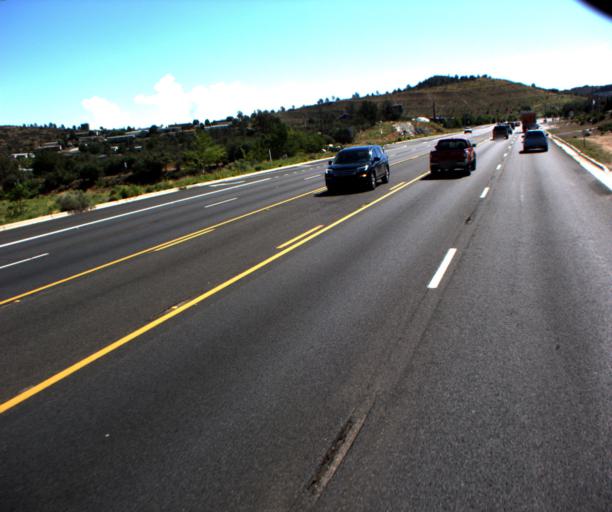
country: US
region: Arizona
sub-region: Yavapai County
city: Prescott
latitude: 34.5526
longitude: -112.4277
